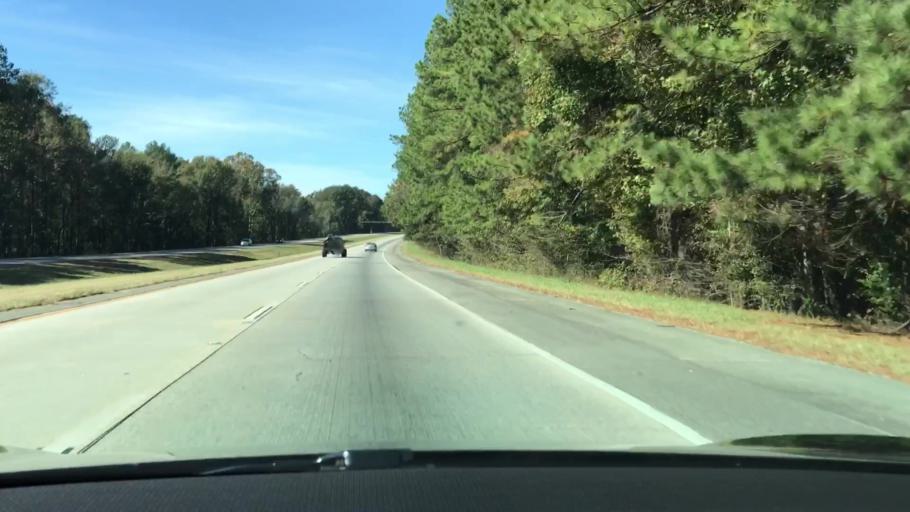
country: US
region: Georgia
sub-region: Taliaferro County
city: Crawfordville
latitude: 33.5280
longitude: -82.9507
